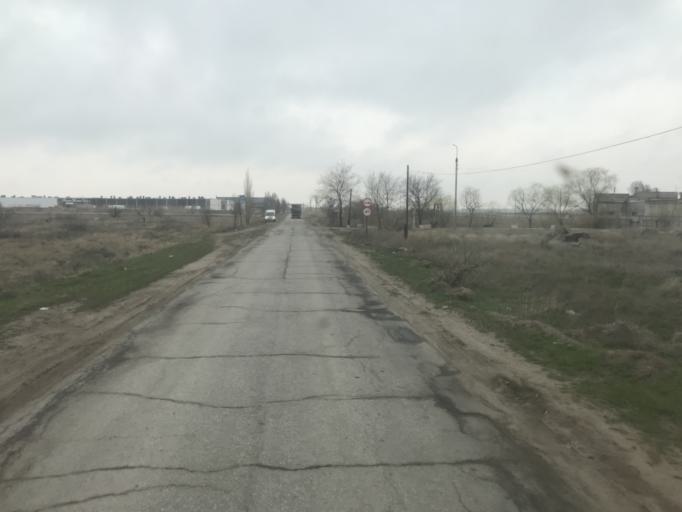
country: RU
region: Volgograd
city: Svetlyy Yar
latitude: 48.5223
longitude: 44.6209
